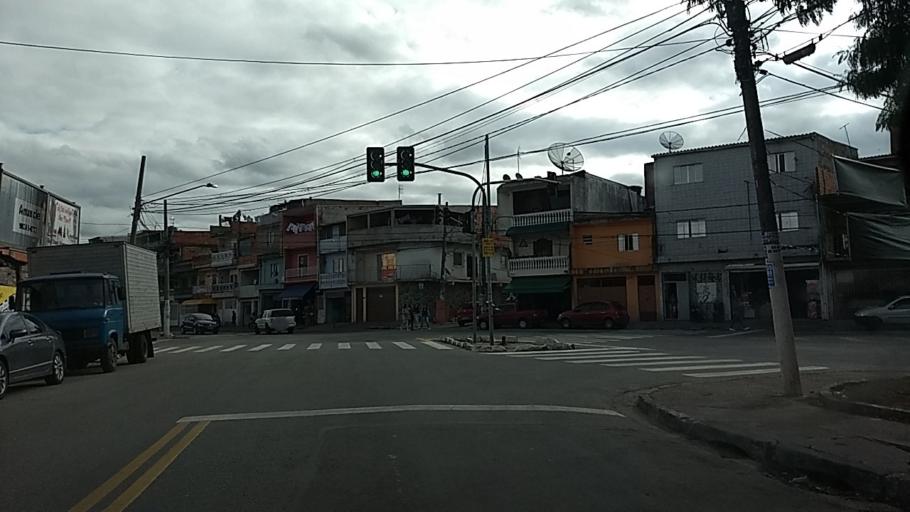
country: BR
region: Sao Paulo
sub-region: Osasco
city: Osasco
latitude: -23.5126
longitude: -46.7817
